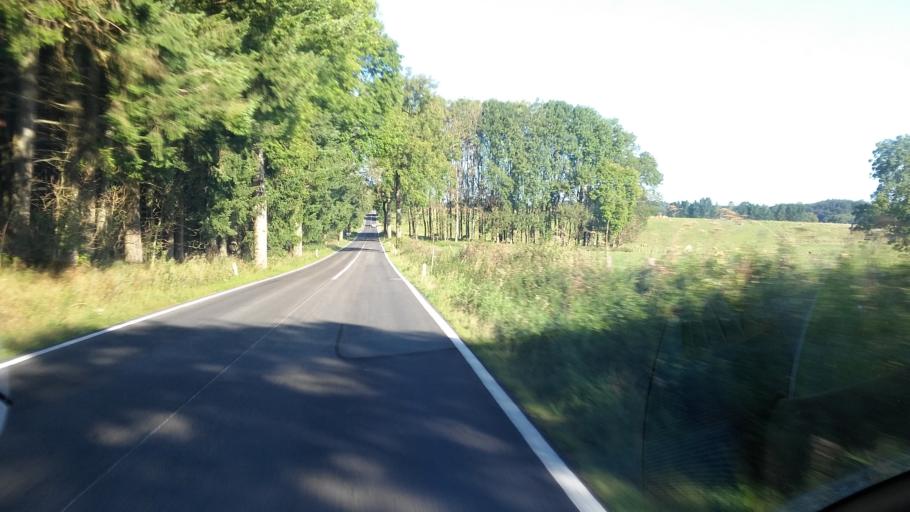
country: BE
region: Wallonia
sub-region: Province du Luxembourg
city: Leglise
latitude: 49.8155
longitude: 5.5009
